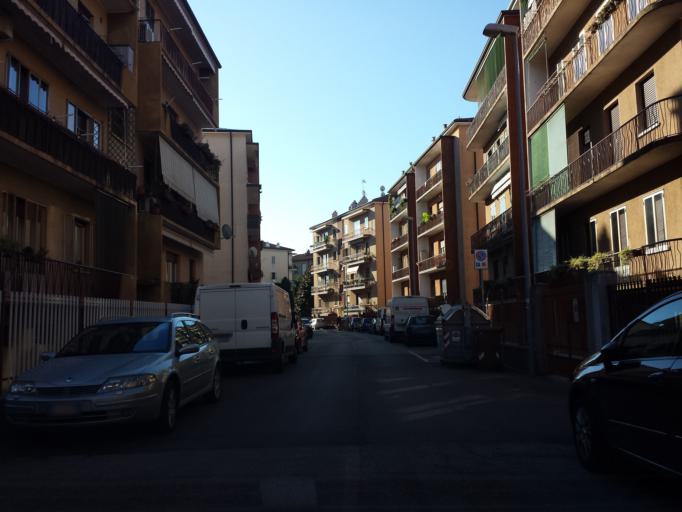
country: IT
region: Veneto
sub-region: Provincia di Vicenza
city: Vicenza
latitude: 45.5610
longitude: 11.5656
